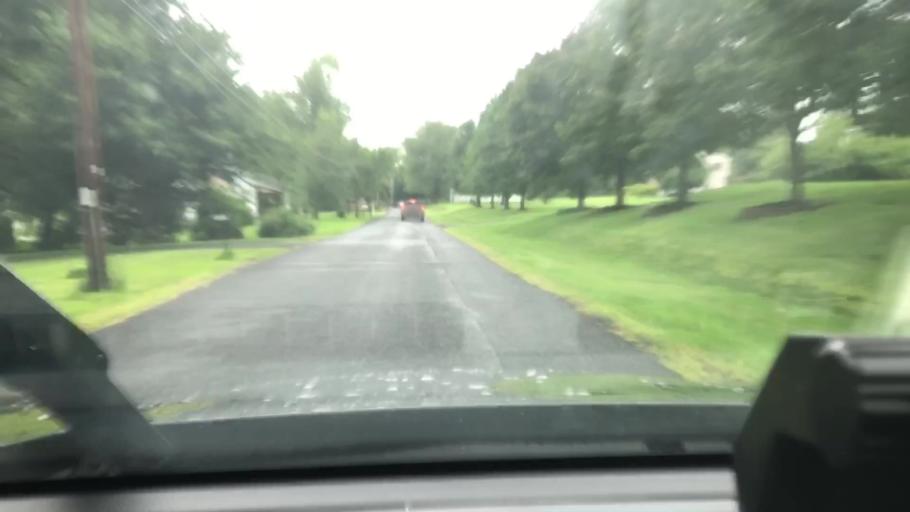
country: US
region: Pennsylvania
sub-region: Lehigh County
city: Coopersburg
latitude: 40.4855
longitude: -75.3969
